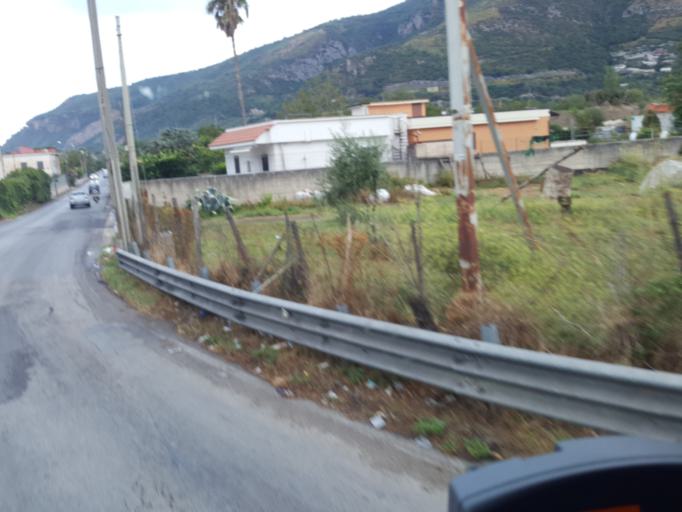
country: IT
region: Campania
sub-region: Provincia di Napoli
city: Striano
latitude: 40.8239
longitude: 14.5987
